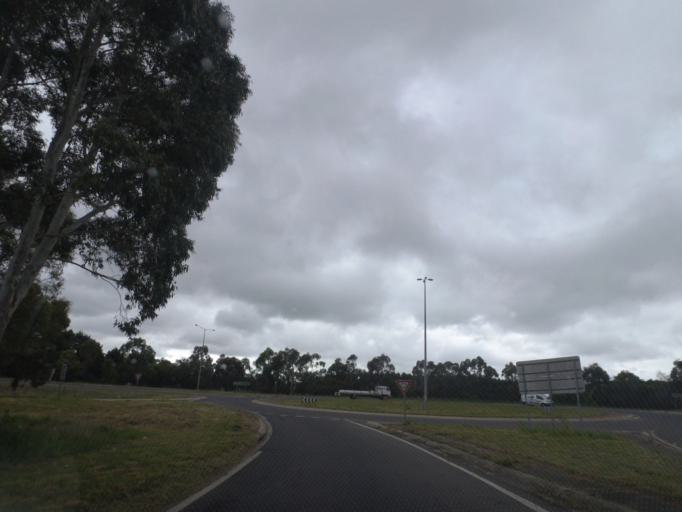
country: AU
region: Victoria
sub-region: Hume
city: Sunbury
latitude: -37.3189
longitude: 144.5274
